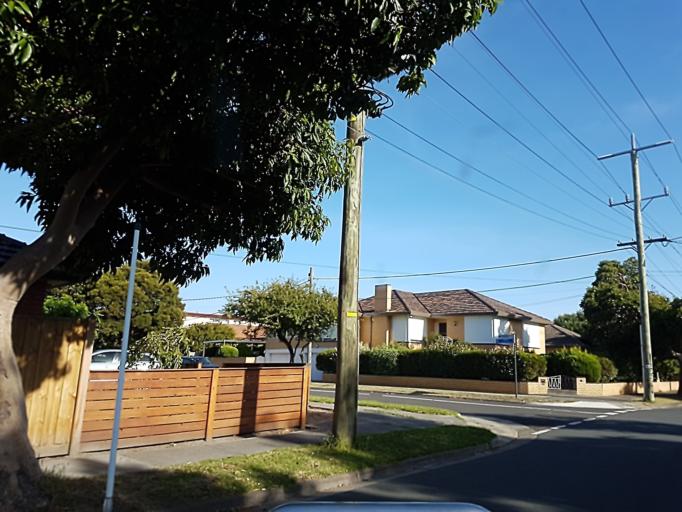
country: AU
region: Victoria
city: Clayton
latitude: -37.9084
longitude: 145.1133
